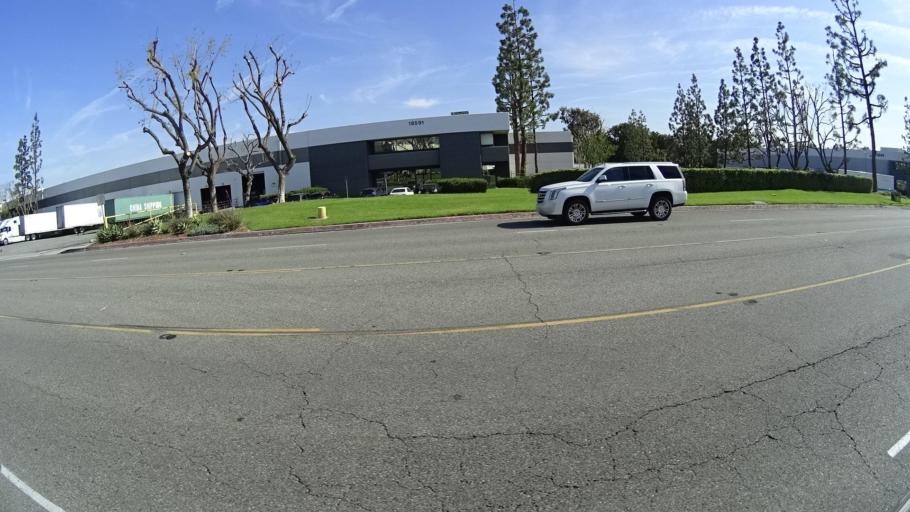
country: US
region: California
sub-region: Los Angeles County
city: South San Jose Hills
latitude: 33.9997
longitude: -117.8996
